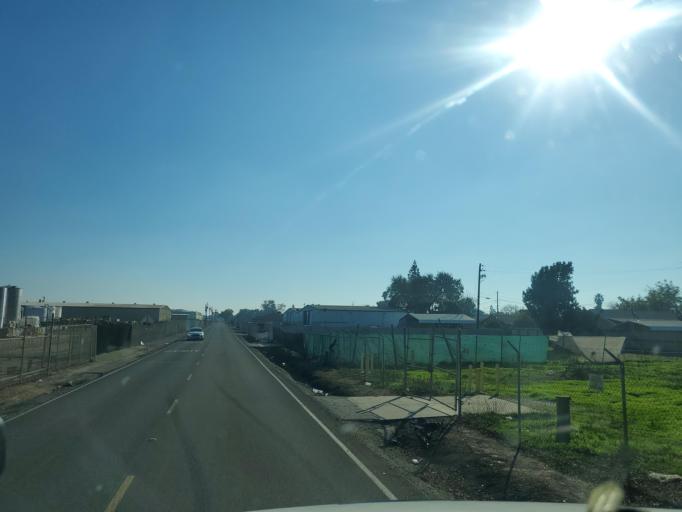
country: US
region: California
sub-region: San Joaquin County
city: August
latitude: 37.9807
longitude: -121.2541
